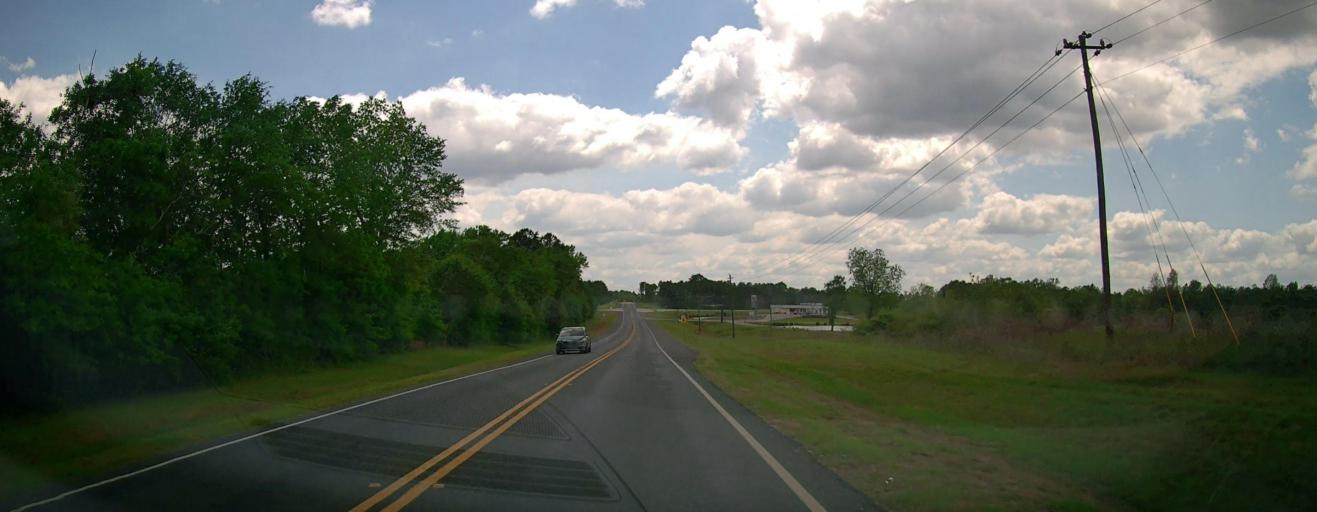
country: US
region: Georgia
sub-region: Treutlen County
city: Soperton
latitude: 32.4398
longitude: -82.6069
